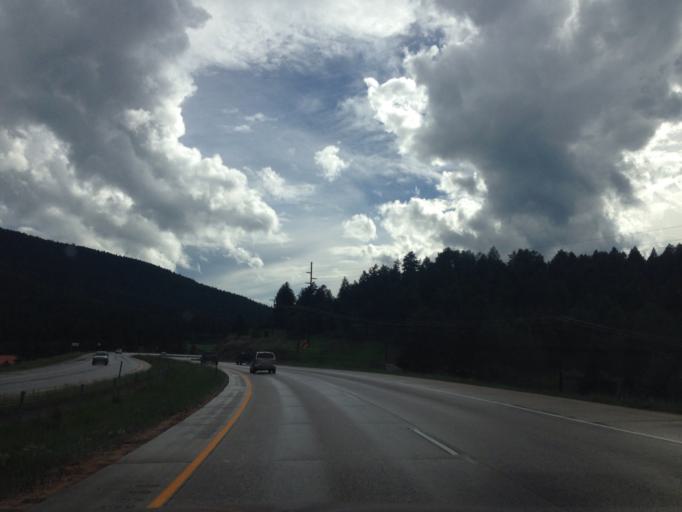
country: US
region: Colorado
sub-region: Jefferson County
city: Indian Hills
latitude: 39.5487
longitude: -105.2657
